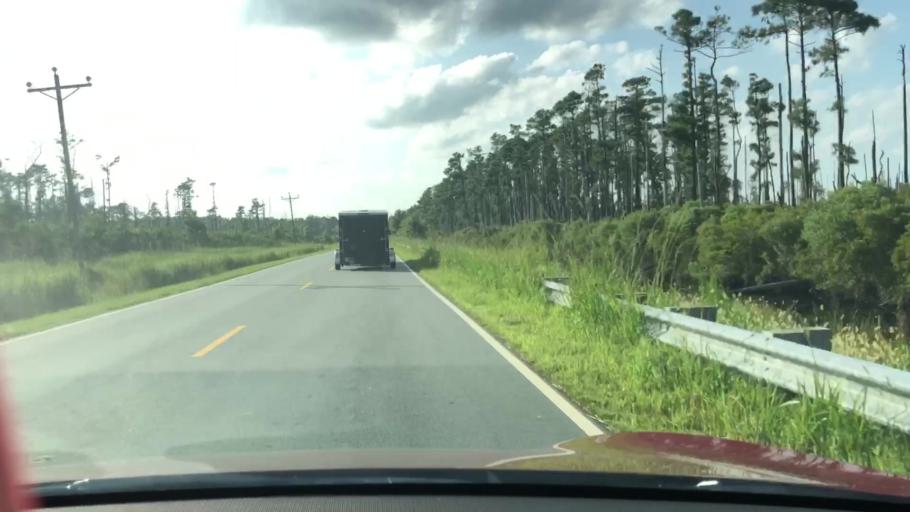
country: US
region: North Carolina
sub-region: Dare County
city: Wanchese
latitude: 35.6103
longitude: -75.8225
